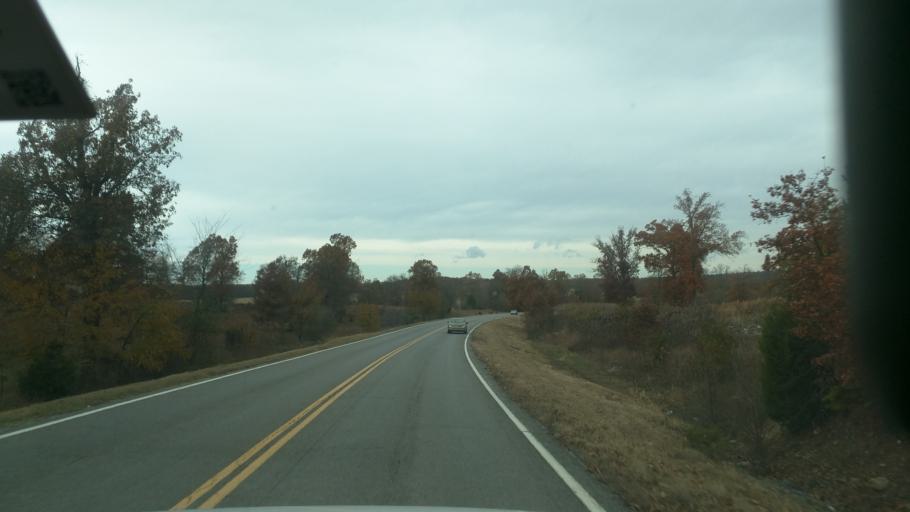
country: US
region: Oklahoma
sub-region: Cherokee County
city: Park Hill
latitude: 35.9036
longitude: -94.8249
